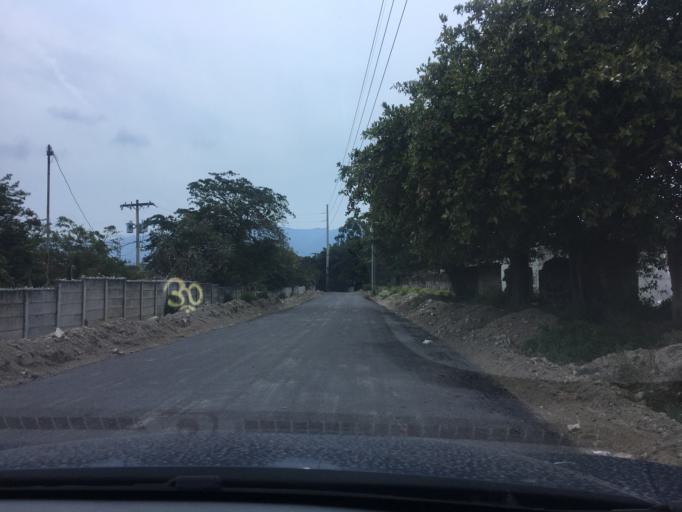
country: GT
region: Guatemala
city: Petapa
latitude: 14.5148
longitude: -90.5520
